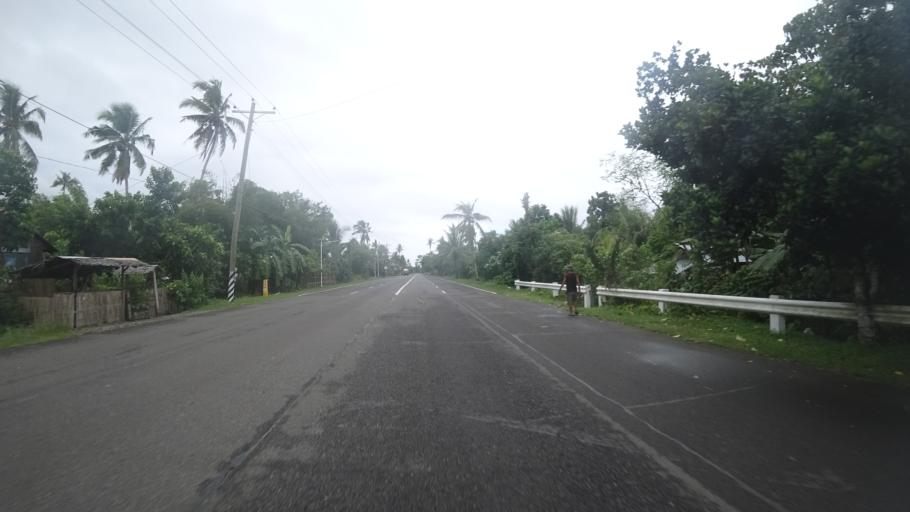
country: PH
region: Eastern Visayas
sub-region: Province of Leyte
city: Mayorga
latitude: 10.8871
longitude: 124.9997
